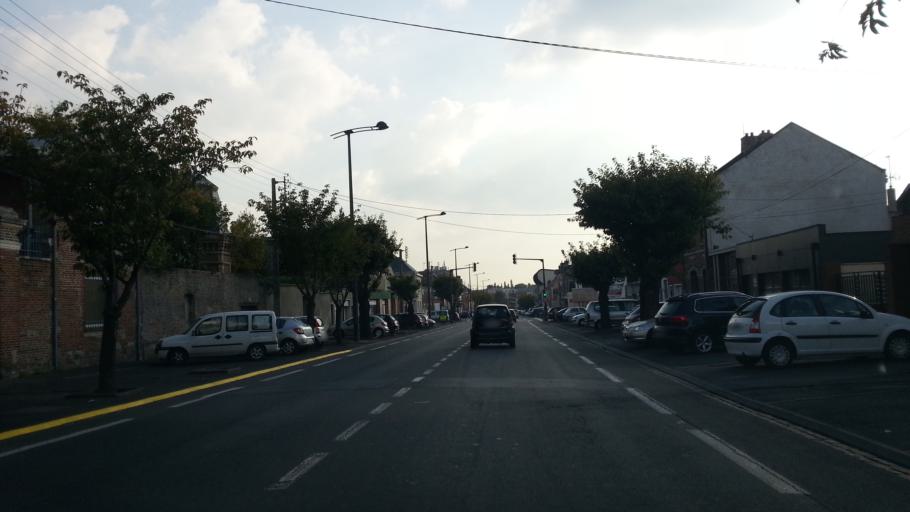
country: FR
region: Picardie
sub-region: Departement de l'Aisne
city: Saint-Quentin
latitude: 49.8466
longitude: 3.2795
